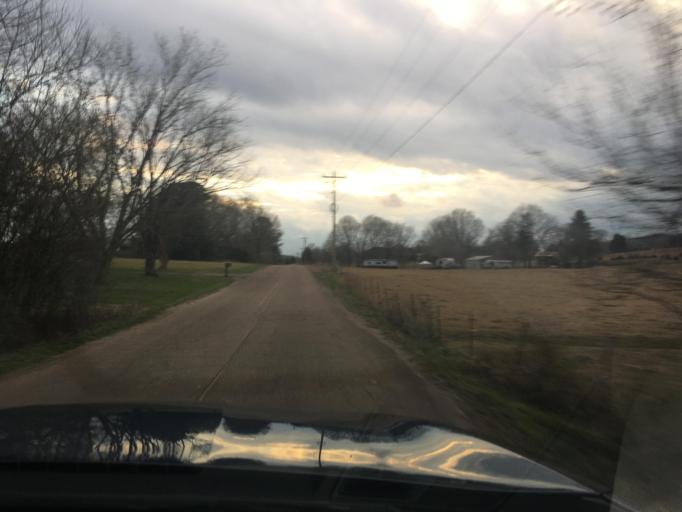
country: US
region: Tennessee
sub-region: Meigs County
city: Decatur
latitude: 35.6012
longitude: -84.6721
